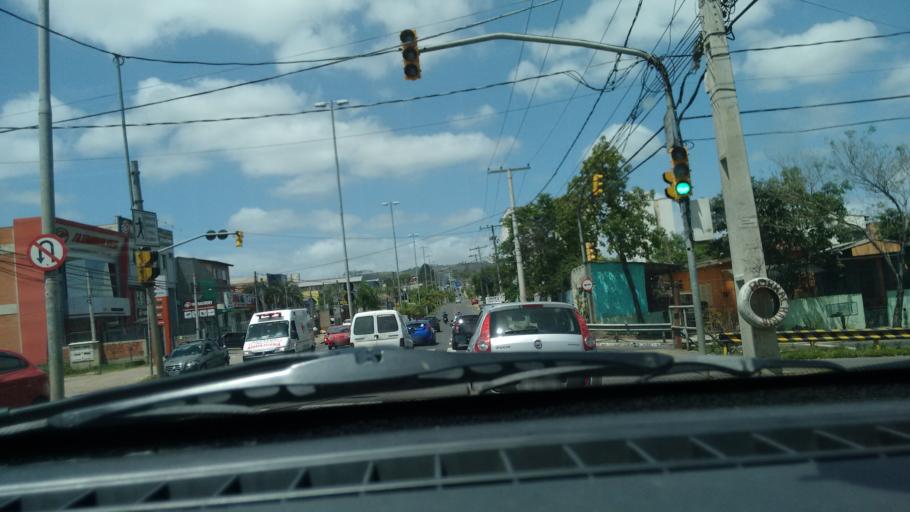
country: BR
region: Rio Grande do Sul
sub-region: Cachoeirinha
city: Cachoeirinha
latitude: -30.0166
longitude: -51.1194
